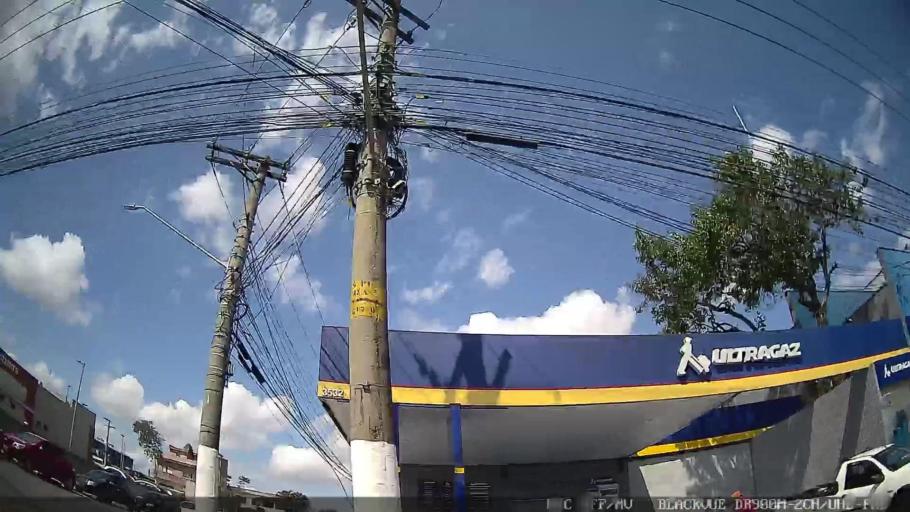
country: BR
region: Sao Paulo
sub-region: Guarulhos
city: Guarulhos
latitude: -23.5150
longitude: -46.4766
